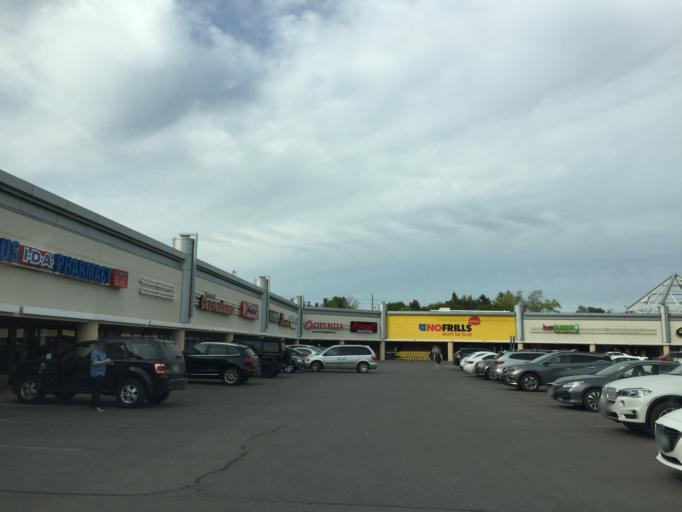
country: CA
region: Ontario
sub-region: Wellington County
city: Guelph
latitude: 43.5245
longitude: -80.2230
